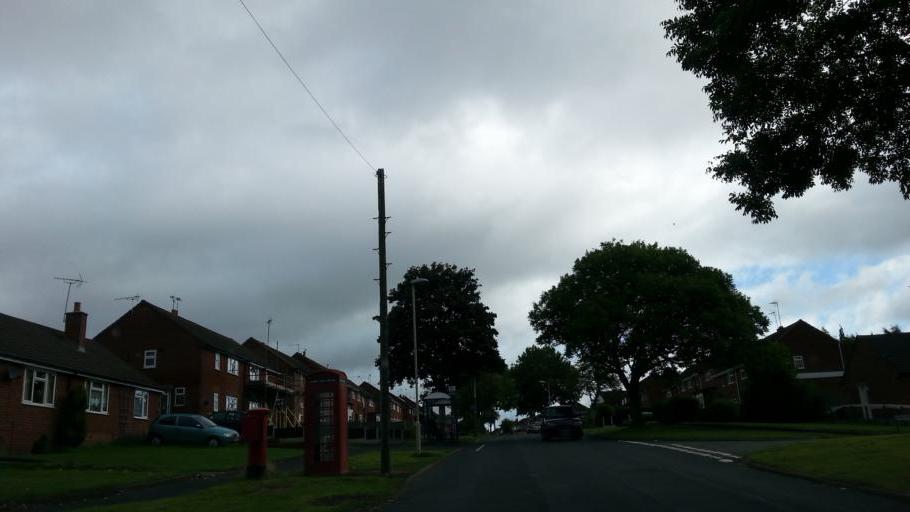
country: GB
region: England
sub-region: Dudley
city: Halesowen
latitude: 52.4424
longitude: -2.0741
